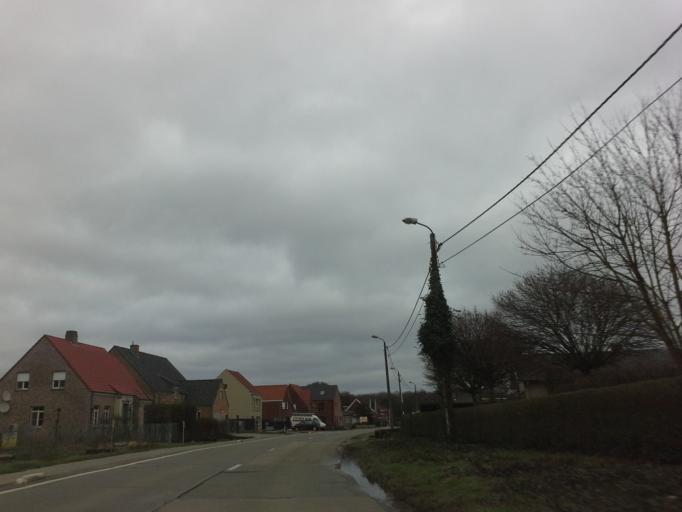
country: BE
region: Flanders
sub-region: Provincie Antwerpen
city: Hulshout
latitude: 51.0854
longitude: 4.7774
